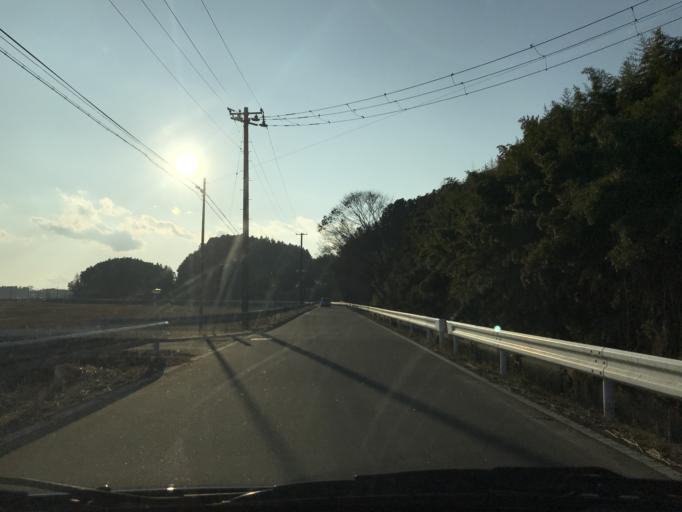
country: JP
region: Miyagi
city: Wakuya
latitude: 38.7155
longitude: 141.1346
